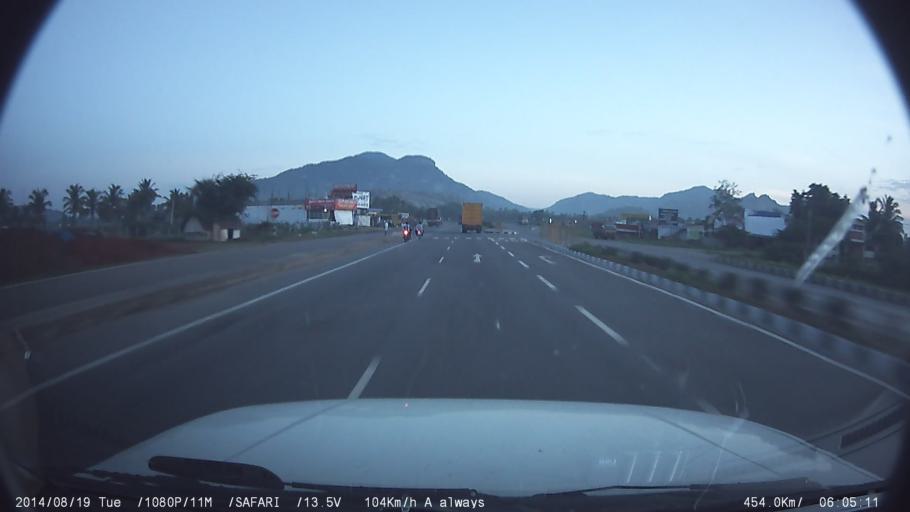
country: IN
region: Tamil Nadu
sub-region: Salem
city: Omalur
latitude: 11.8748
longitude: 78.0827
